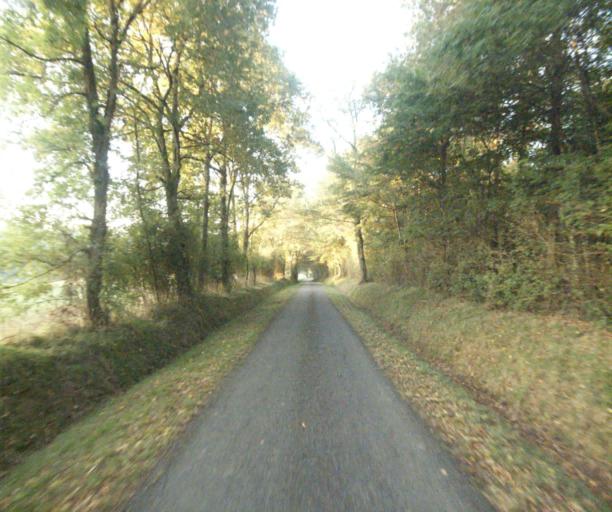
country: FR
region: Midi-Pyrenees
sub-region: Departement du Gers
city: Gondrin
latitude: 43.7949
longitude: 0.1846
